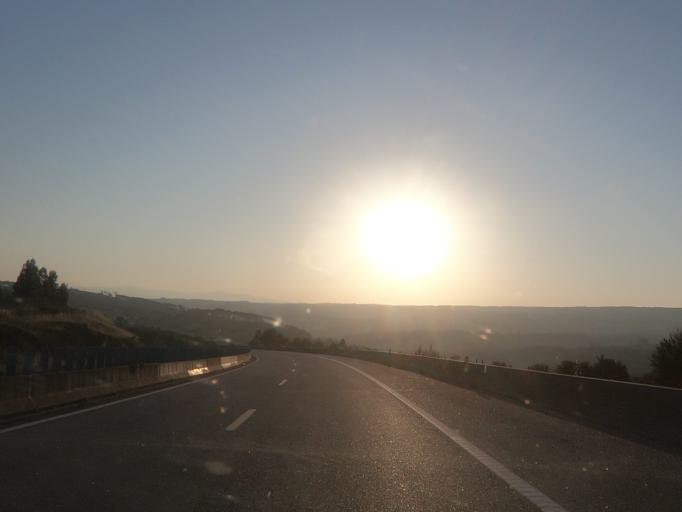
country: PT
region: Viseu
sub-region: Mangualde
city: Mangualde
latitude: 40.6278
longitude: -7.7885
